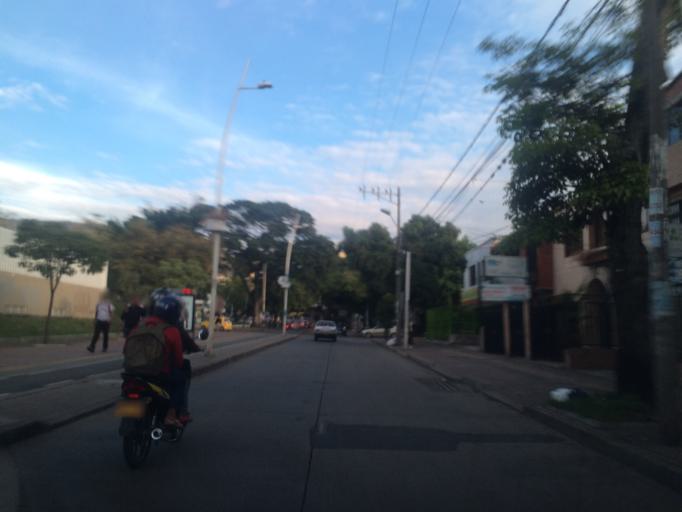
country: CO
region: Valle del Cauca
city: Cali
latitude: 3.4311
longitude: -76.5411
